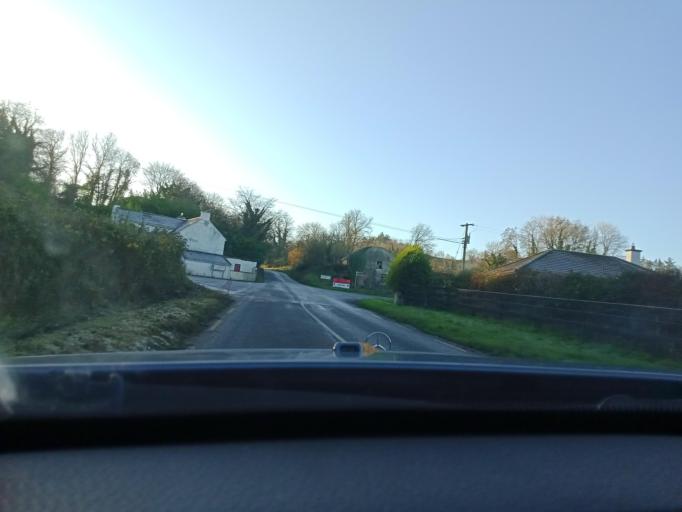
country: IE
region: Leinster
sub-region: Kilkenny
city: Callan
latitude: 52.4675
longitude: -7.3966
